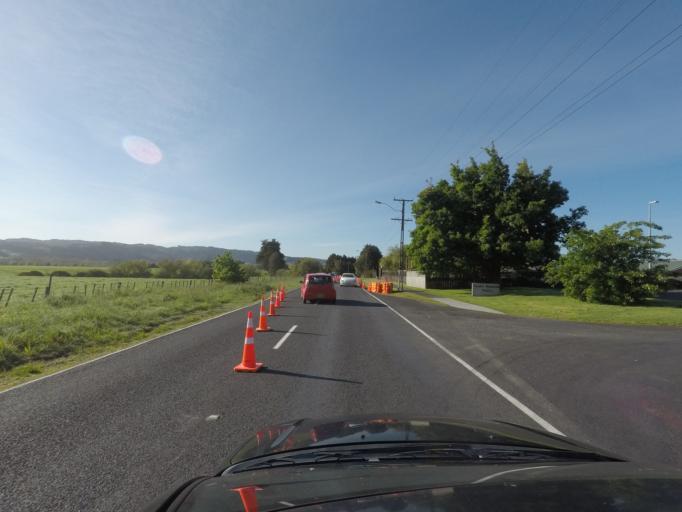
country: NZ
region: Auckland
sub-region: Auckland
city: Red Hill
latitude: -37.0004
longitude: 175.0400
